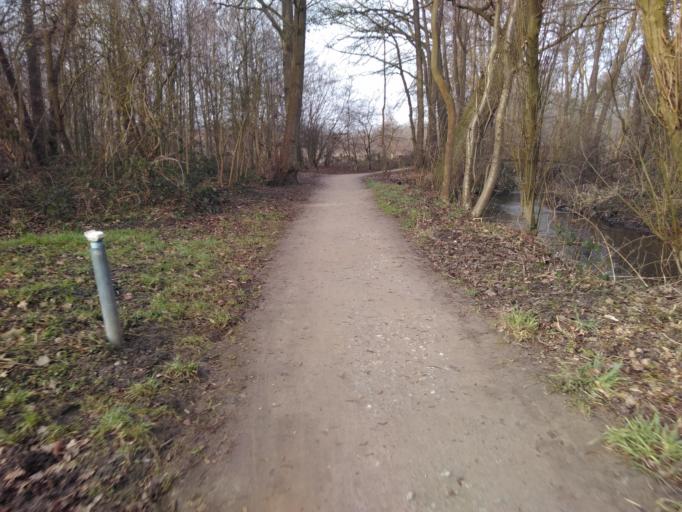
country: DE
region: North Rhine-Westphalia
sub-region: Regierungsbezirk Detmold
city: Verl
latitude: 51.8864
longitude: 8.4869
